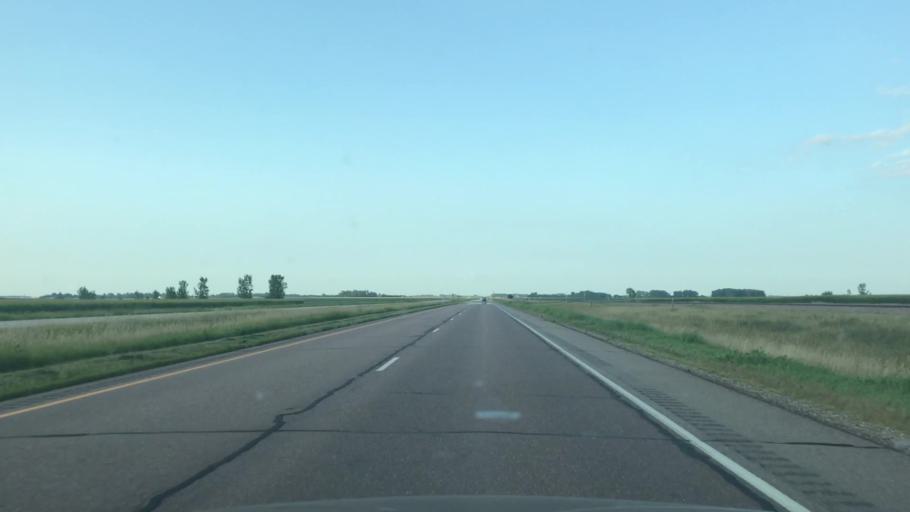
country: US
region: Minnesota
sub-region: Nobles County
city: Worthington
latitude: 43.7299
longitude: -95.4233
